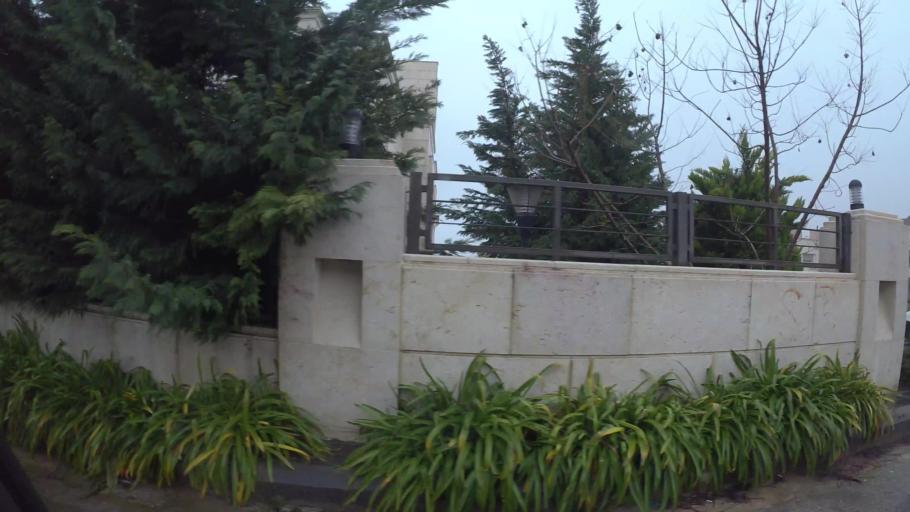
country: JO
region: Amman
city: Al Jubayhah
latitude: 32.0123
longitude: 35.8358
